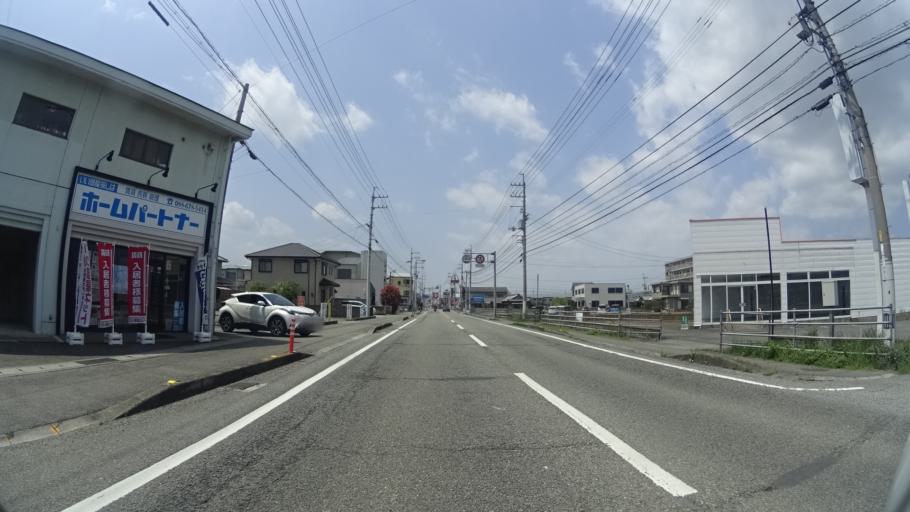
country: JP
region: Tokushima
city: Ishii
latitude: 34.0697
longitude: 134.4547
